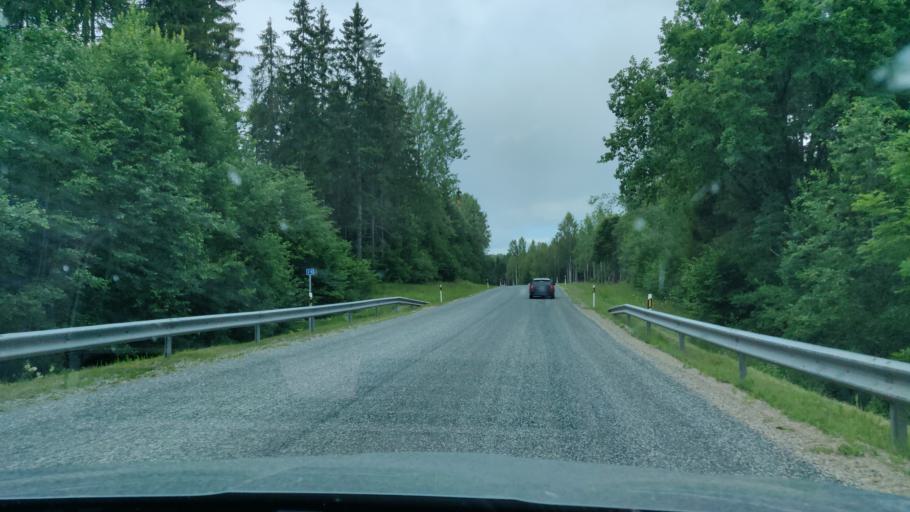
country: EE
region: Vorumaa
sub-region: Antsla vald
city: Vana-Antsla
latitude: 58.0264
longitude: 26.5778
